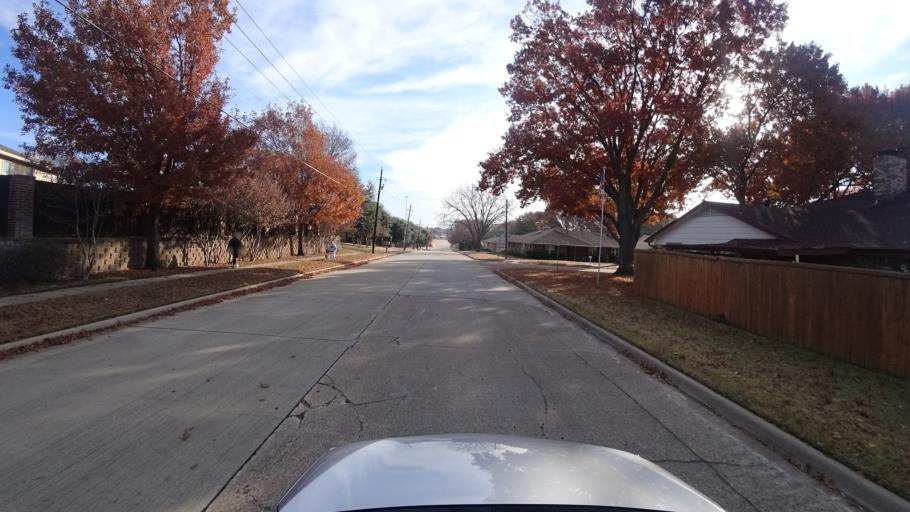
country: US
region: Texas
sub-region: Collin County
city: McKinney
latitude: 33.2042
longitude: -96.6430
